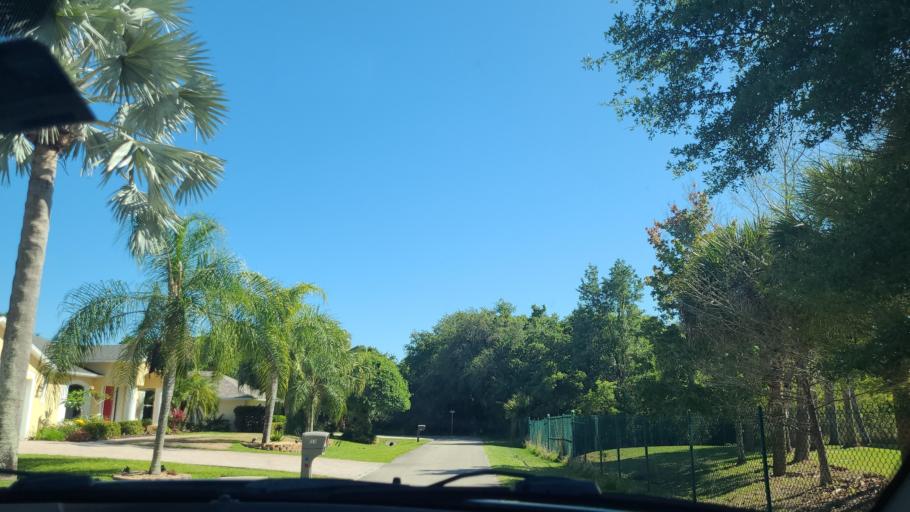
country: US
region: Florida
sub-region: Indian River County
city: Sebastian
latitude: 27.7685
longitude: -80.5029
